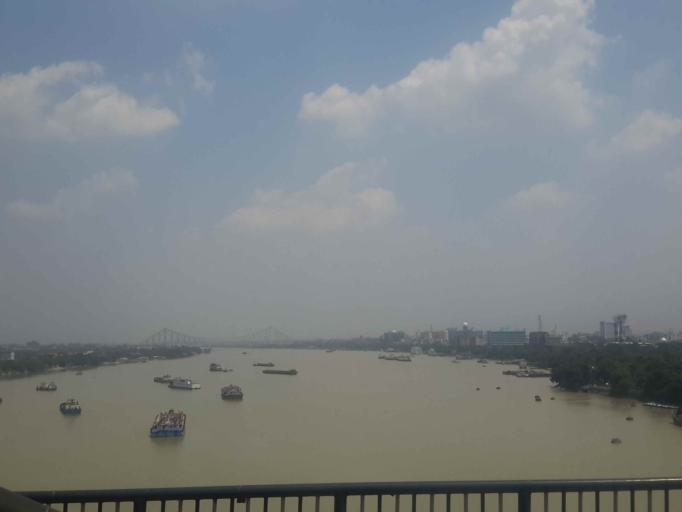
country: IN
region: West Bengal
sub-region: Haora
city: Haora
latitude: 22.5569
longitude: 88.3282
